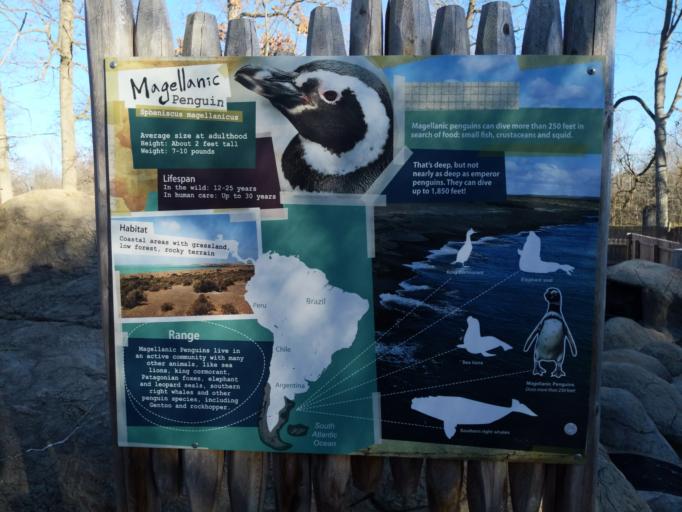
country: US
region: Michigan
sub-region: Ingham County
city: Lansing
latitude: 42.7177
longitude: -84.5240
